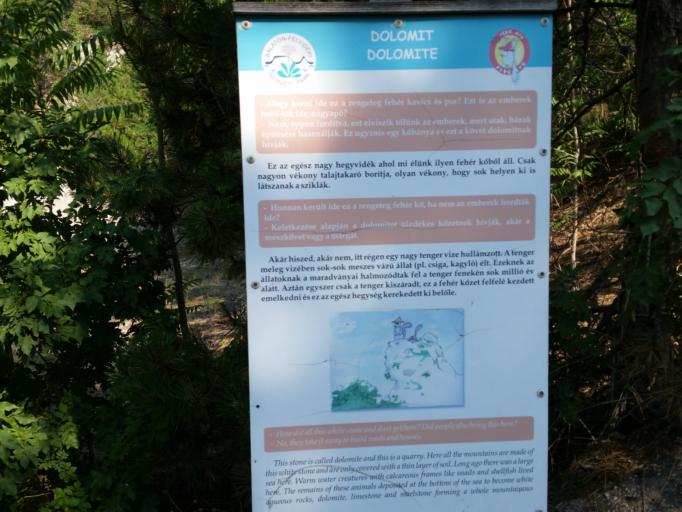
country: HU
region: Zala
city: Vonyarcvashegy
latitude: 46.7713
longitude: 17.3583
